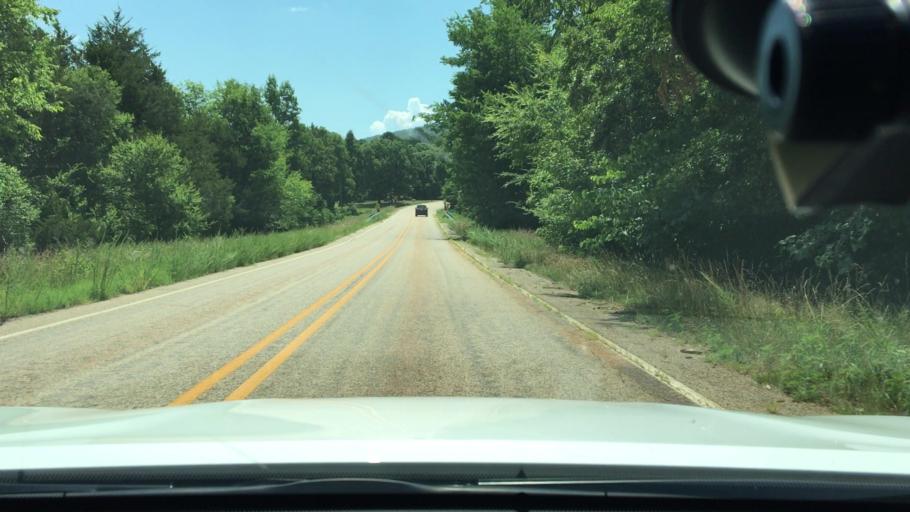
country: US
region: Arkansas
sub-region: Logan County
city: Paris
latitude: 35.1911
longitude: -93.6246
